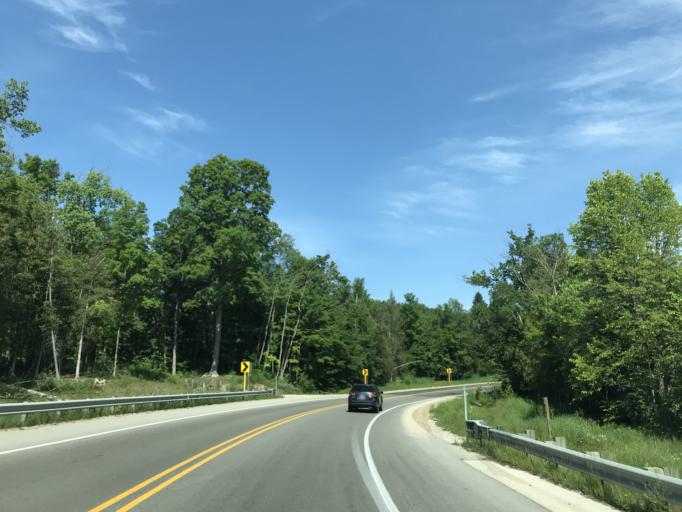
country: US
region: Michigan
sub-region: Grand Traverse County
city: Traverse City
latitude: 44.6989
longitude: -85.6245
